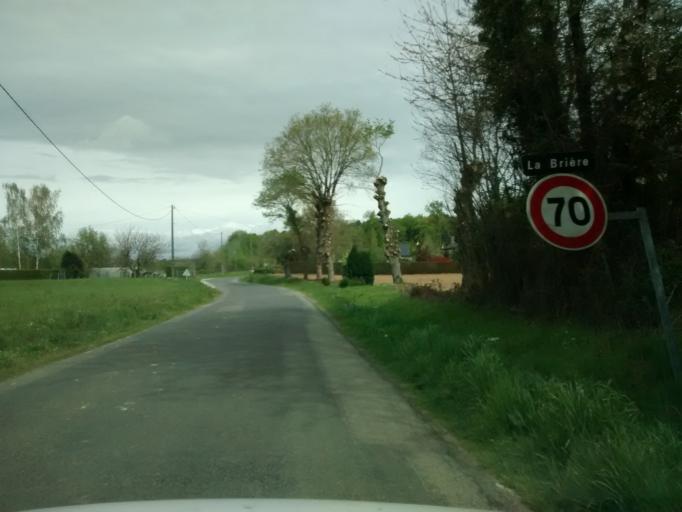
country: FR
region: Brittany
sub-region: Departement du Morbihan
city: Ruffiac
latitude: 47.8016
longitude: -2.3243
